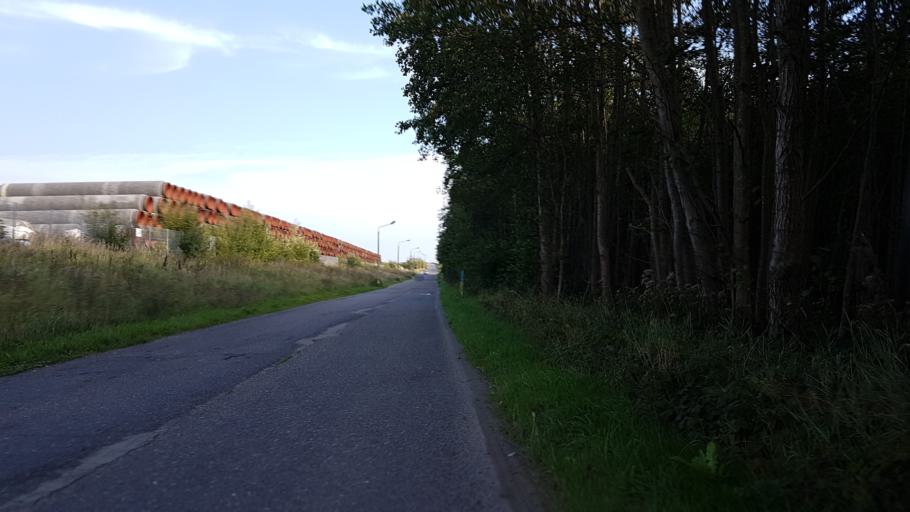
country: DE
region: Mecklenburg-Vorpommern
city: Sagard
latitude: 54.4904
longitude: 13.5715
